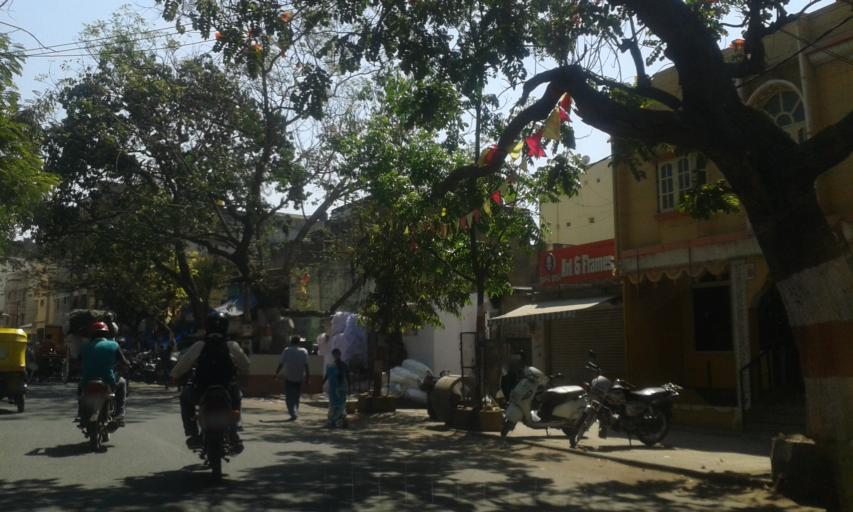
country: IN
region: Karnataka
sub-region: Bangalore Urban
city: Bangalore
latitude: 12.9689
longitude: 77.5675
